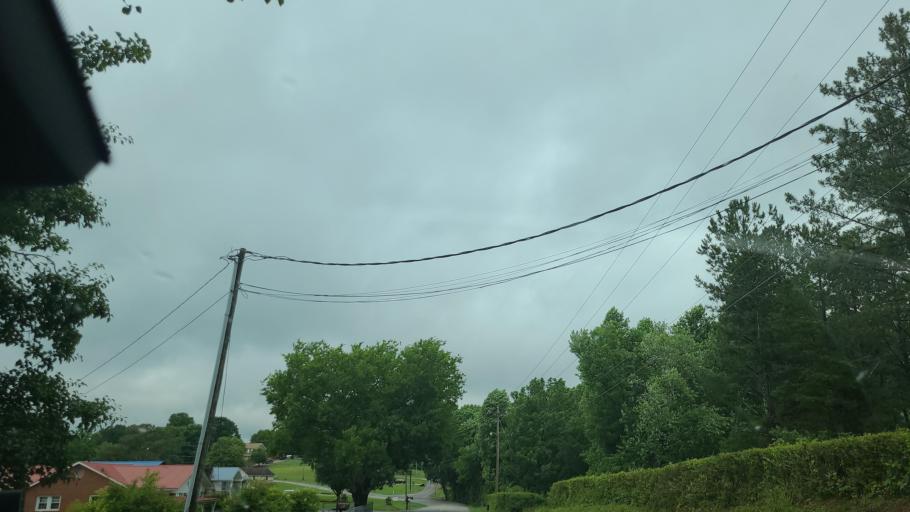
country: US
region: Tennessee
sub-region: Rhea County
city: Dayton
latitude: 35.5062
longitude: -84.9879
